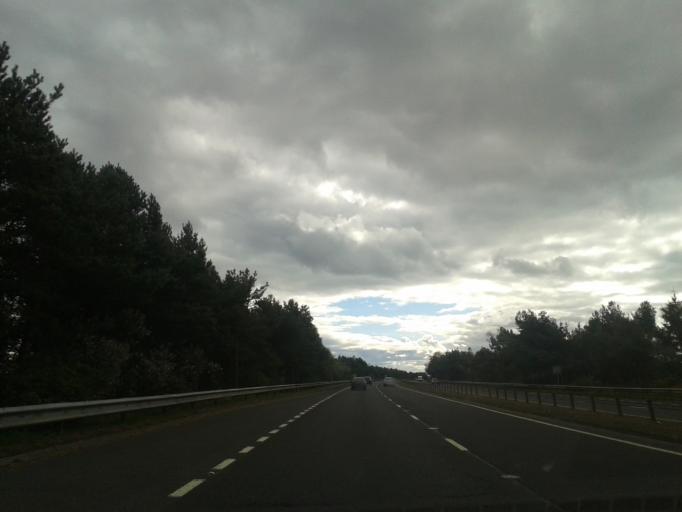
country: GB
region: Scotland
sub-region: Fife
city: Thornton
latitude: 56.1701
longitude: -3.1384
